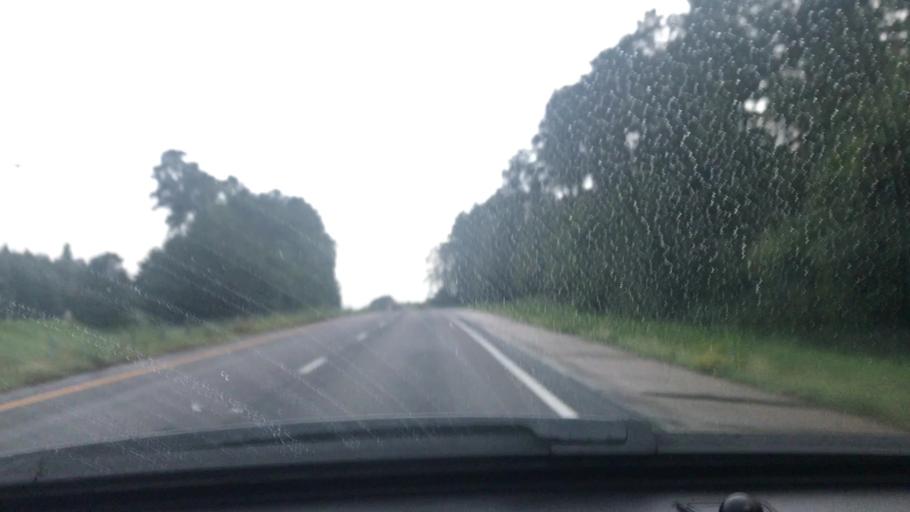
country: US
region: Mississippi
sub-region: Pike County
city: Magnolia
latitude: 31.1043
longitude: -90.4868
